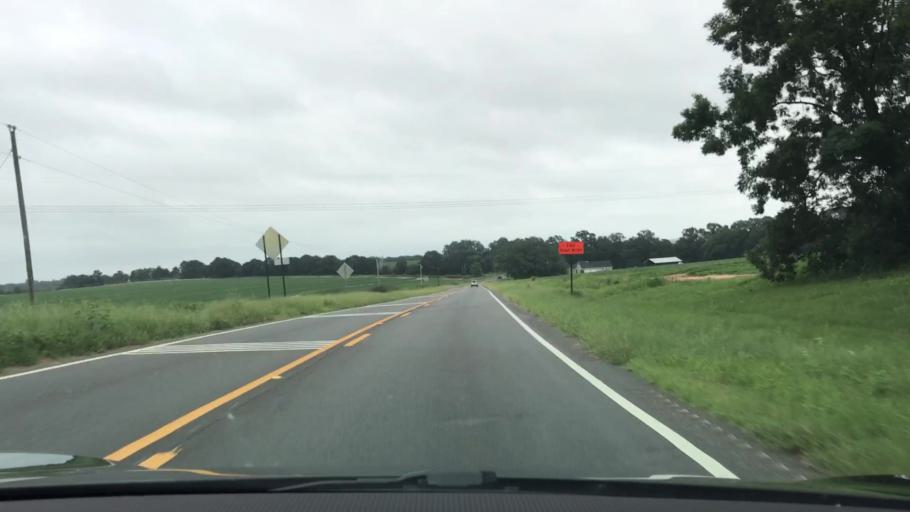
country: US
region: Alabama
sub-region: Covington County
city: Opp
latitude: 31.2816
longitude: -86.1562
